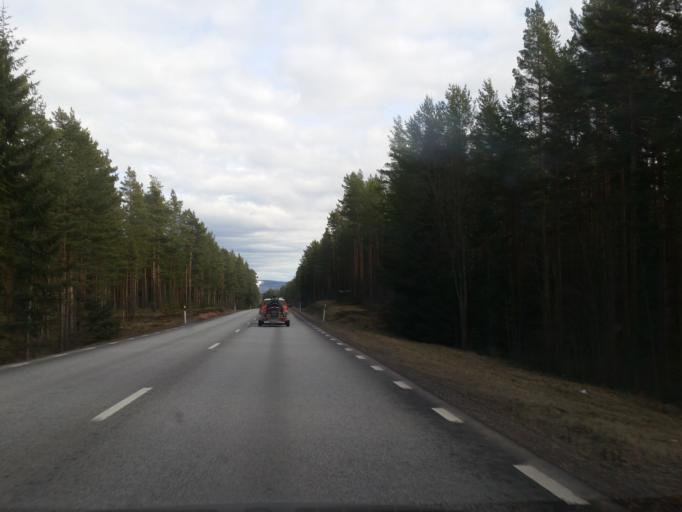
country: SE
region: Dalarna
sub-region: Rattviks Kommun
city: Vikarbyn
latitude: 60.9066
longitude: 14.9340
